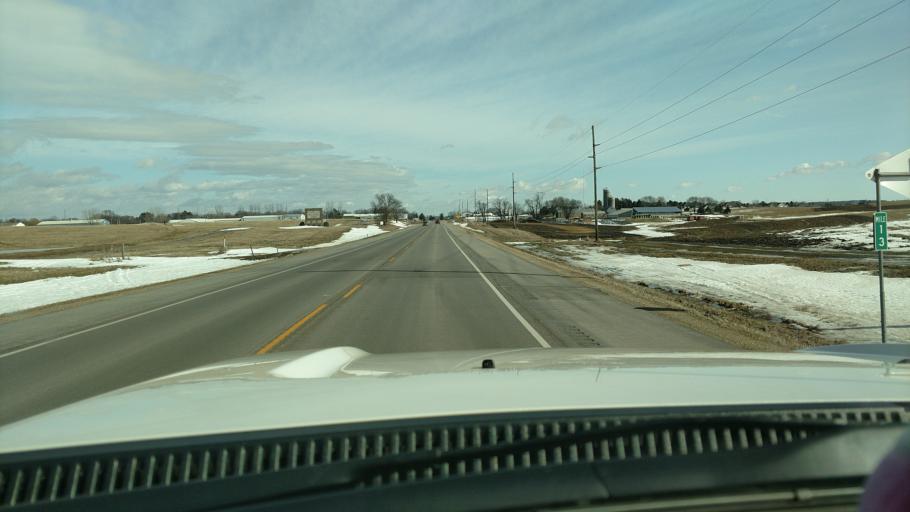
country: US
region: Minnesota
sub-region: Wabasha County
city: Plainview
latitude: 44.1580
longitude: -92.1879
